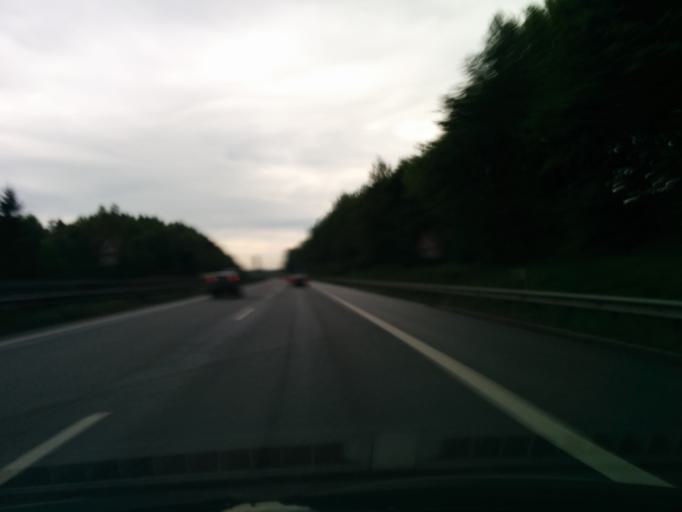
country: DE
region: Lower Saxony
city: Seevetal
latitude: 53.4308
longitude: 9.9408
